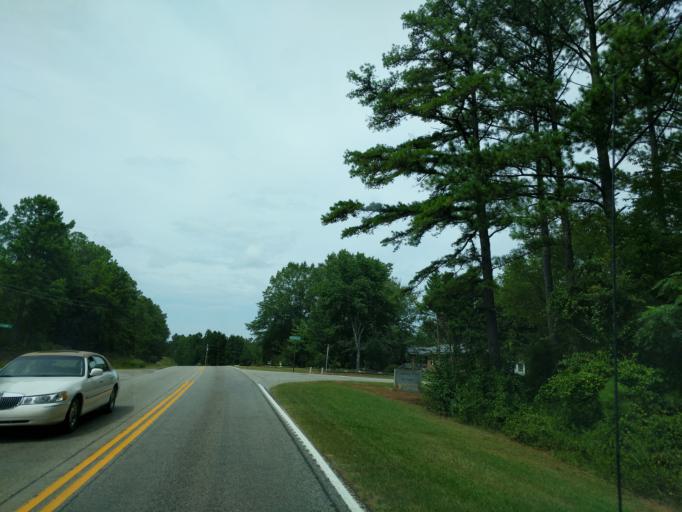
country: US
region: South Carolina
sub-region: Abbeville County
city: Calhoun Falls
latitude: 34.1169
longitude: -82.5961
